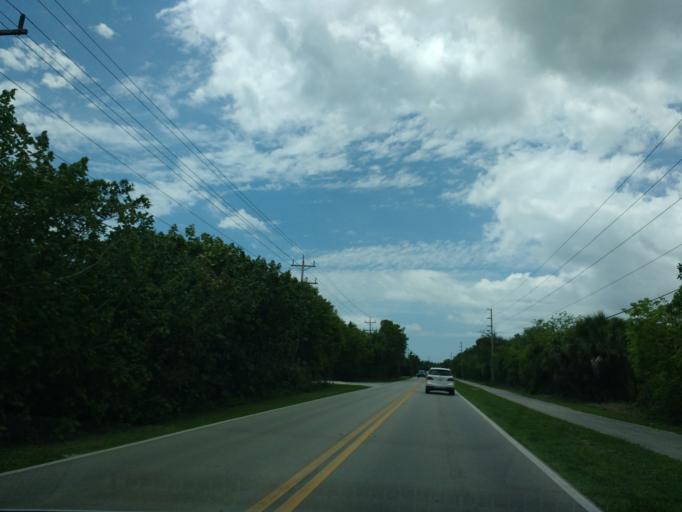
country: US
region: Florida
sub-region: Lee County
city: Saint James City
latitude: 26.4497
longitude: -82.1238
